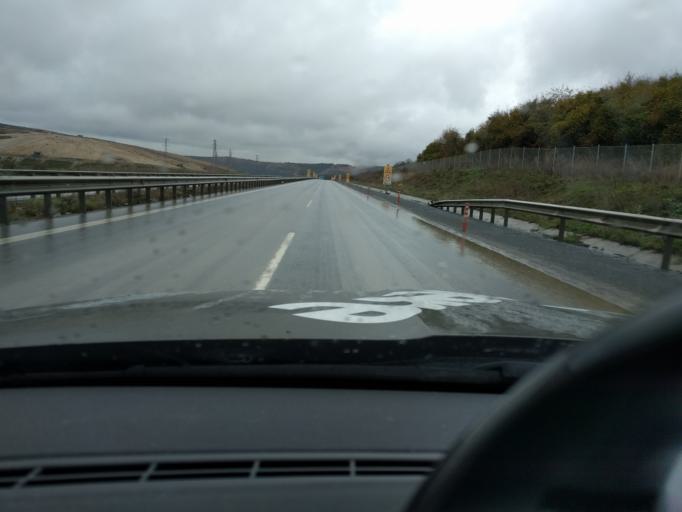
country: TR
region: Istanbul
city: Kemerburgaz
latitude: 41.2273
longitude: 28.8447
